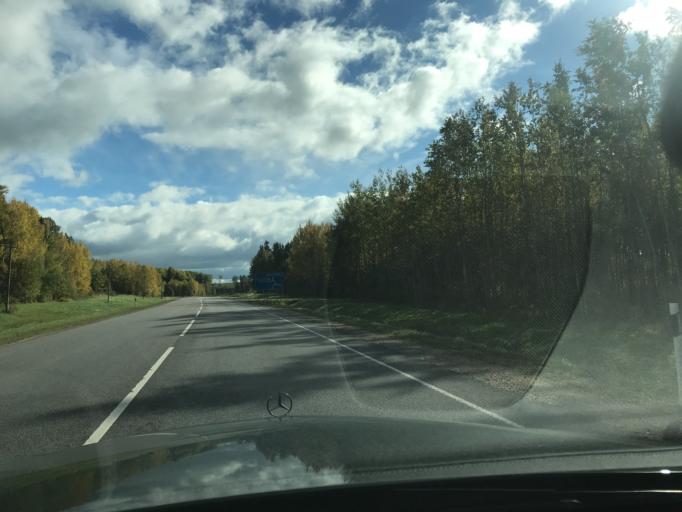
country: EE
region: Vorumaa
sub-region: Voru linn
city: Voru
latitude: 57.8516
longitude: 27.0314
